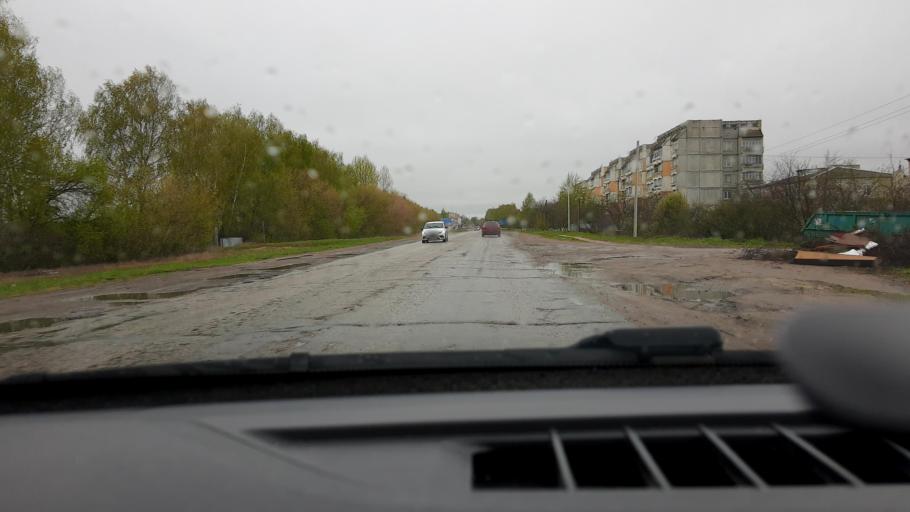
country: RU
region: Nizjnij Novgorod
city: Perevoz
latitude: 55.5982
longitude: 44.5686
